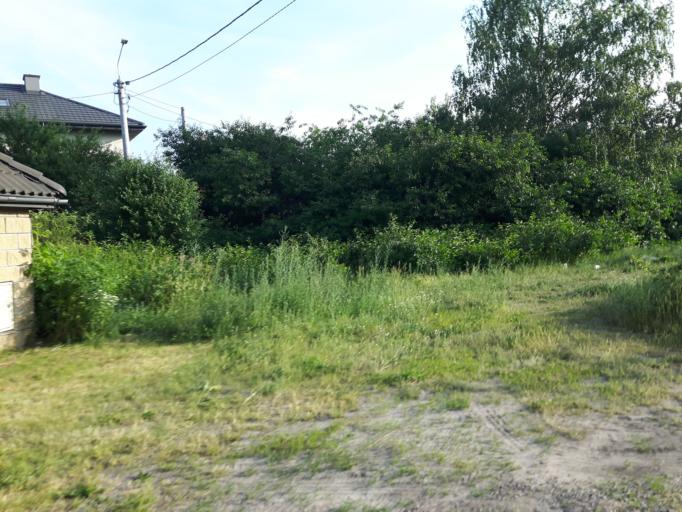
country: PL
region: Masovian Voivodeship
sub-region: Powiat wolominski
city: Zabki
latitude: 52.2820
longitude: 21.1326
